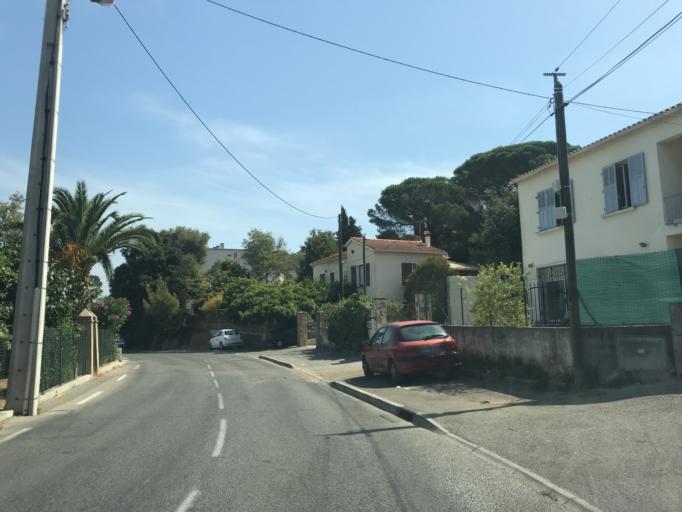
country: FR
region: Provence-Alpes-Cote d'Azur
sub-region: Departement du Var
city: La Seyne-sur-Mer
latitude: 43.0918
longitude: 5.8782
